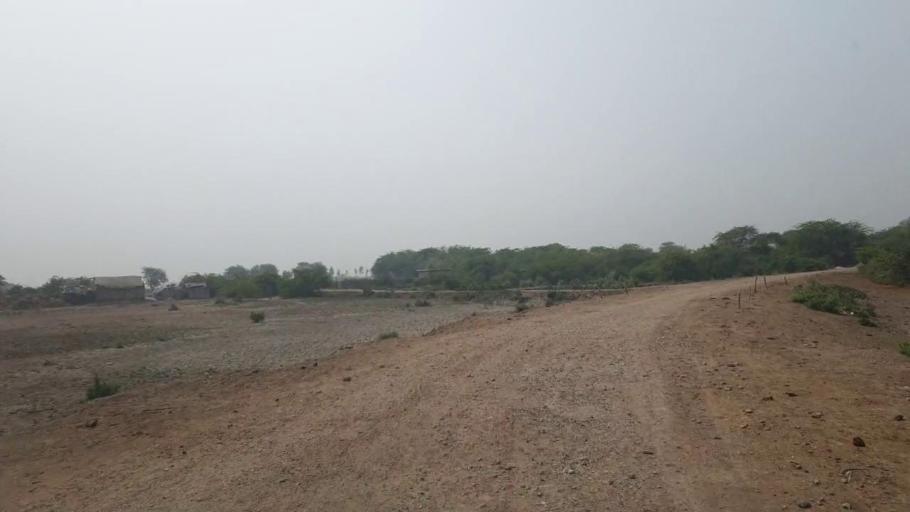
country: PK
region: Sindh
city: Kario
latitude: 24.6530
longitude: 68.6629
